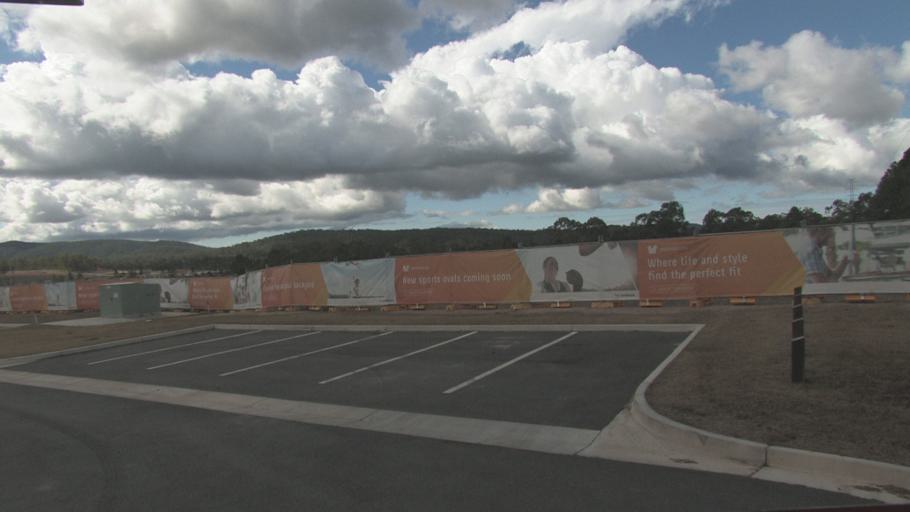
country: AU
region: Queensland
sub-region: Logan
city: Chambers Flat
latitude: -27.8128
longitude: 153.1158
